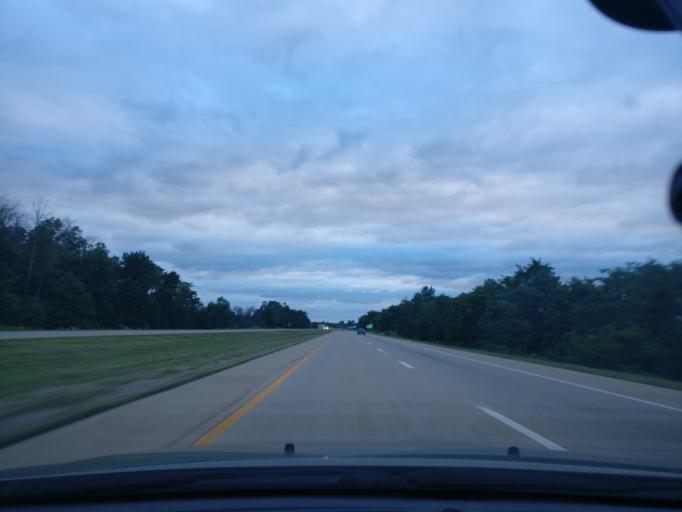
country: US
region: Ohio
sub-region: Greene County
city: Wilberforce
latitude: 39.6891
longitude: -83.8663
